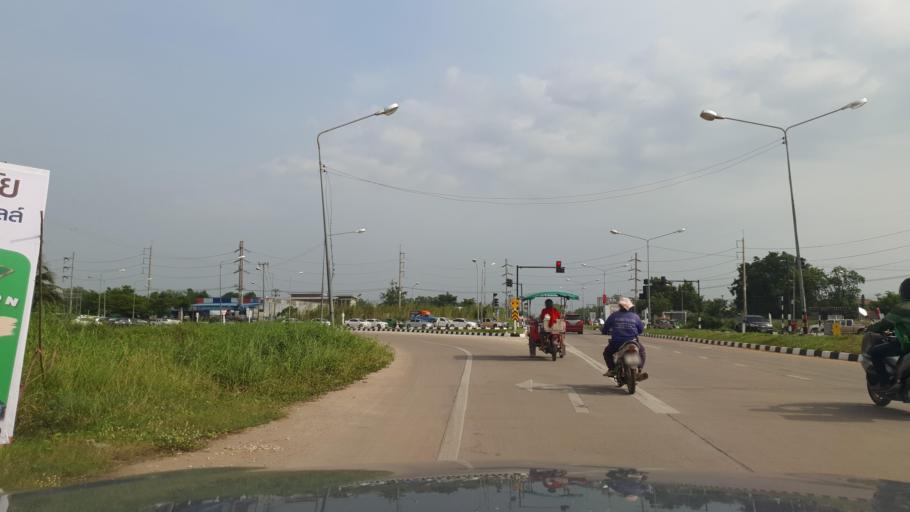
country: TH
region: Phitsanulok
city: Phitsanulok
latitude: 16.8640
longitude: 100.2499
